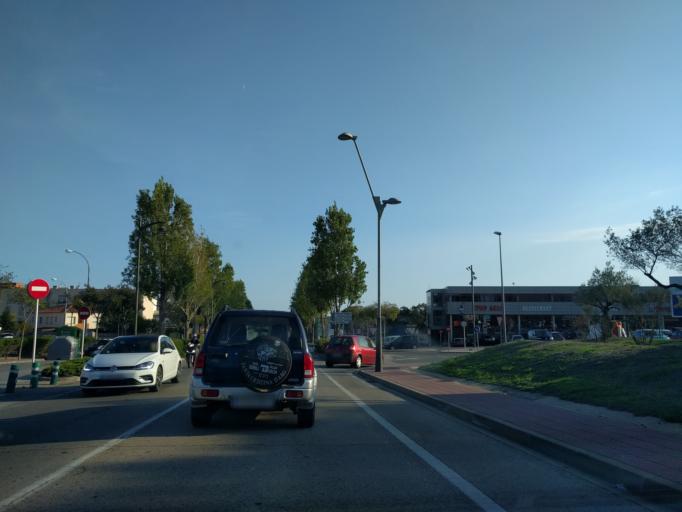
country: ES
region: Catalonia
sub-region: Provincia de Girona
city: Sant Feliu de Guixols
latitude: 41.7947
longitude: 3.0199
